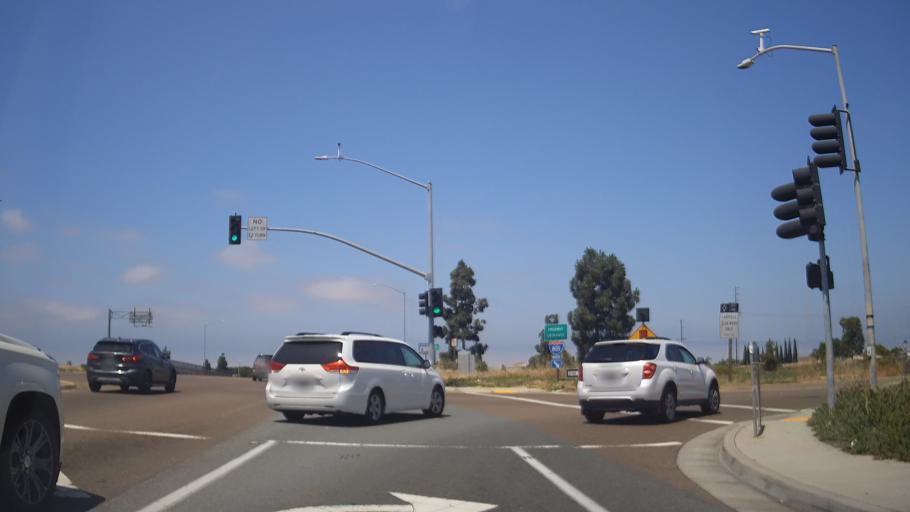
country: US
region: California
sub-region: San Diego County
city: Bonita
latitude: 32.6063
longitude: -117.0349
